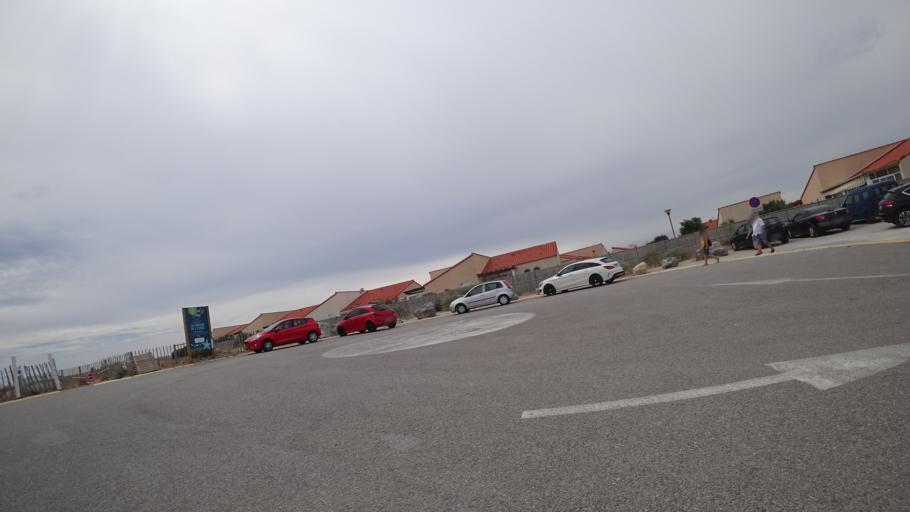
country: FR
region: Languedoc-Roussillon
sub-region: Departement de l'Aude
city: Leucate
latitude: 42.8847
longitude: 3.0507
